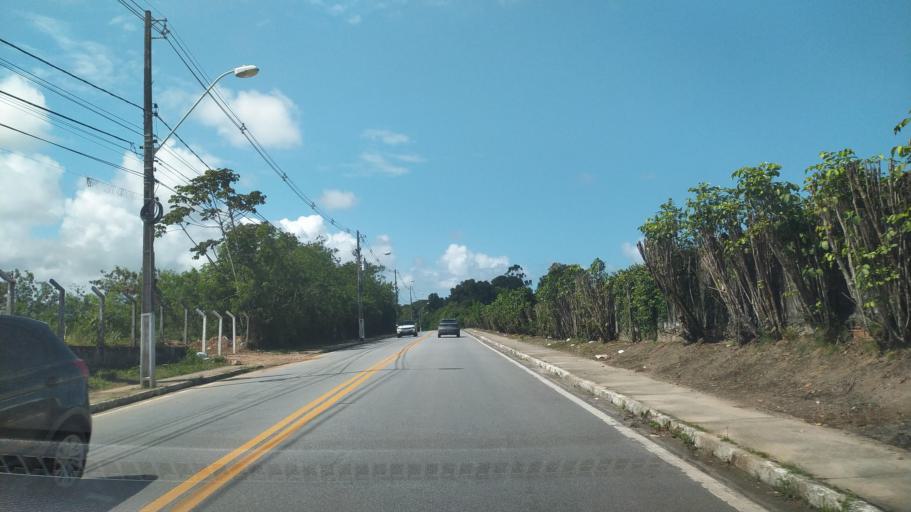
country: BR
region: Alagoas
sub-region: Maceio
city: Maceio
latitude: -9.6028
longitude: -35.7412
